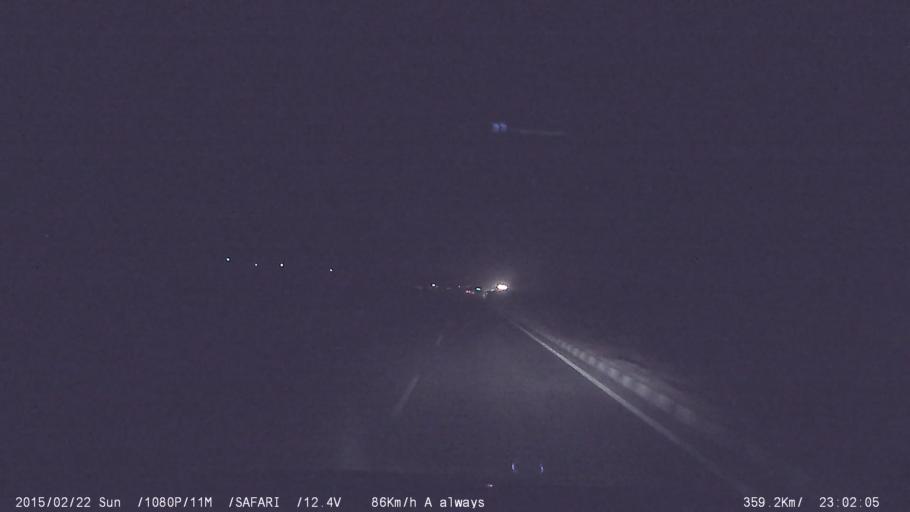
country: IN
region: Tamil Nadu
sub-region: Namakkal
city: Rasipuram
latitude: 11.3719
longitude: 78.1634
